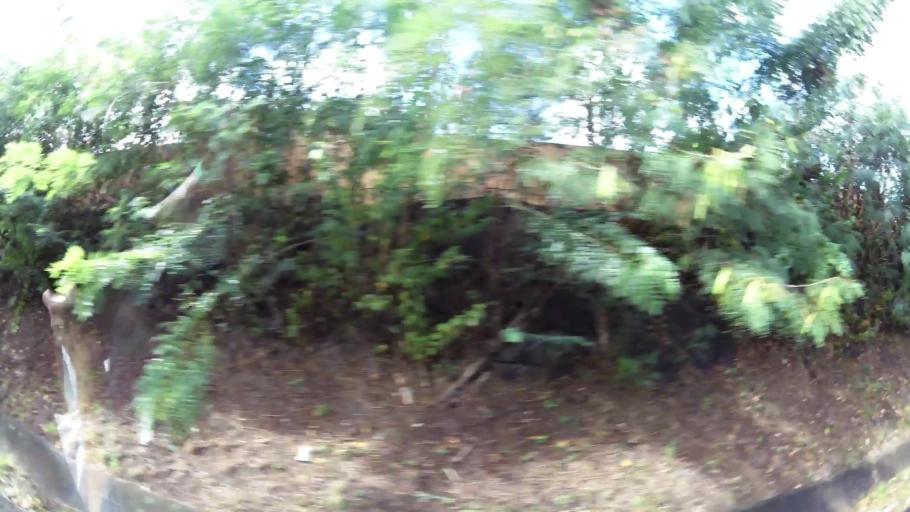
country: MQ
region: Martinique
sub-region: Martinique
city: Les Trois-Ilets
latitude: 14.5487
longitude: -61.0499
